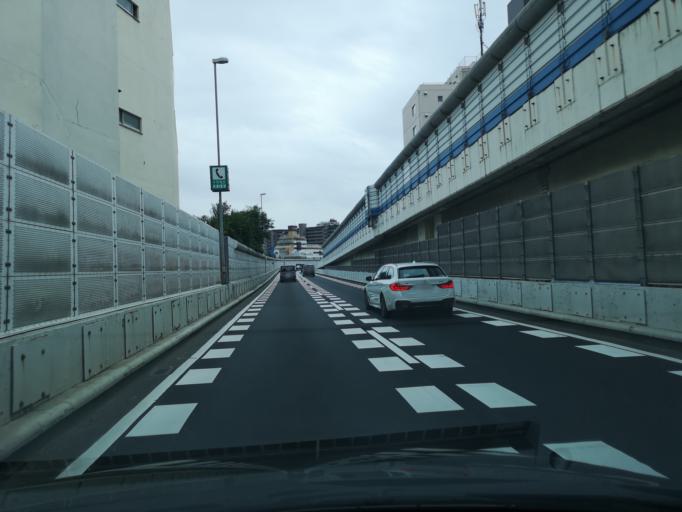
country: JP
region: Tokyo
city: Tokyo
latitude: 35.6515
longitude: 139.7374
